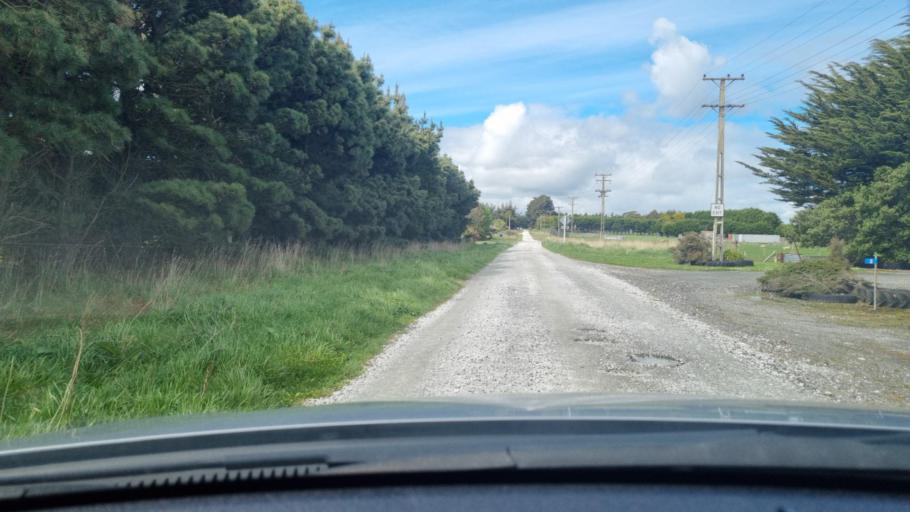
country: NZ
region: Southland
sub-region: Invercargill City
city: Invercargill
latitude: -46.4745
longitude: 168.3868
